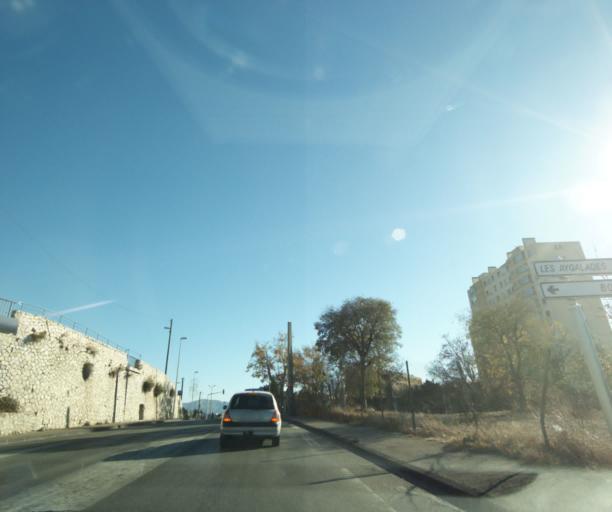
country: FR
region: Provence-Alpes-Cote d'Azur
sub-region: Departement des Bouches-du-Rhone
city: Marseille 15
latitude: 43.3590
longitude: 5.3650
